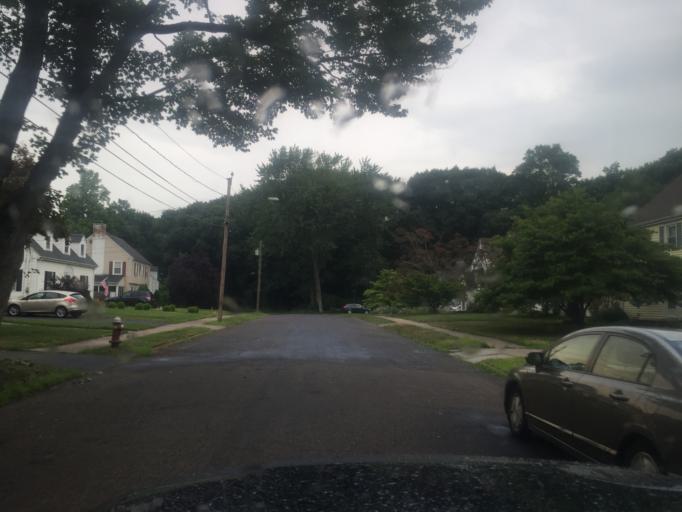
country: US
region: Connecticut
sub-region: Hartford County
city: New Britain
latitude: 41.6962
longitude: -72.7686
